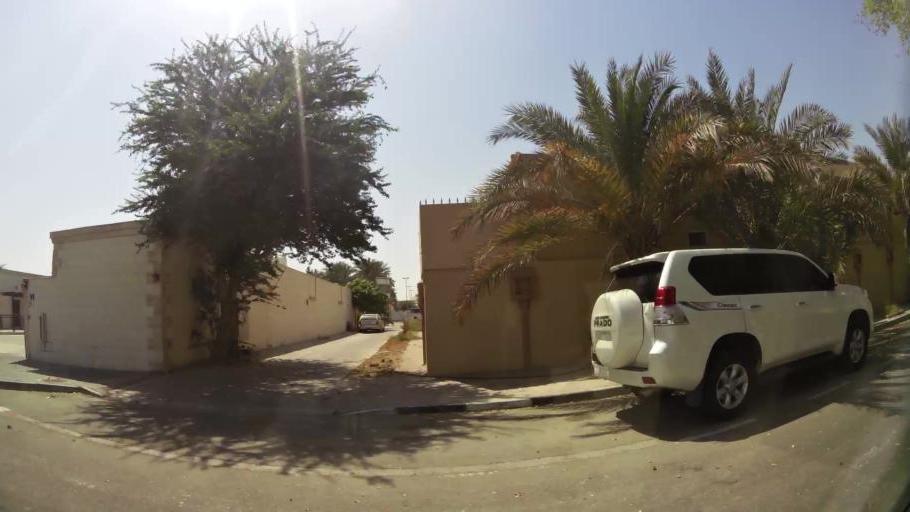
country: AE
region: Ash Shariqah
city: Sharjah
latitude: 25.2717
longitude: 55.3658
